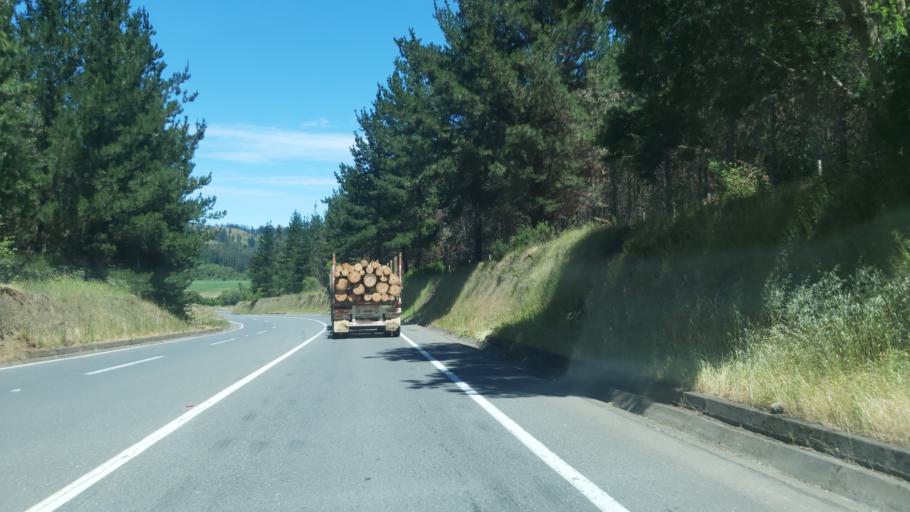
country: CL
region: Maule
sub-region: Provincia de Talca
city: Constitucion
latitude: -35.1526
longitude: -72.2205
